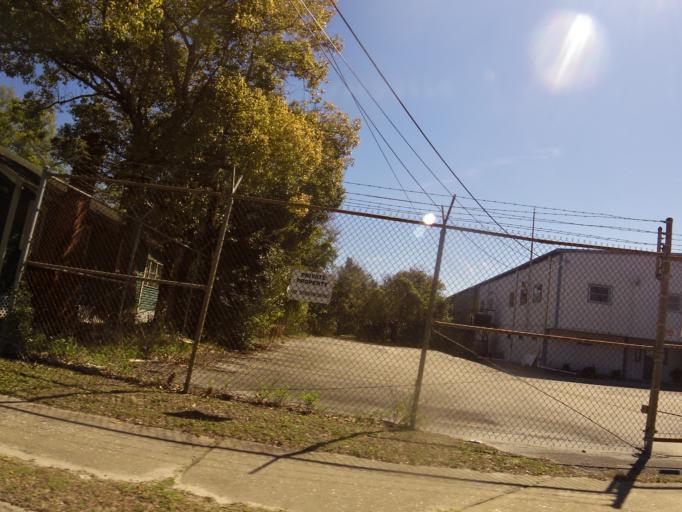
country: US
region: Florida
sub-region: Duval County
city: Jacksonville
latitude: 30.3604
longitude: -81.6426
